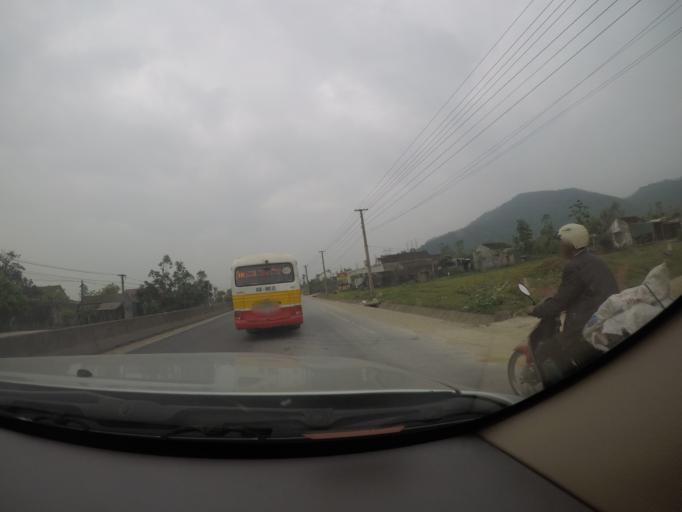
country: VN
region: Ha Tinh
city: Ky Anh
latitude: 18.1379
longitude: 106.2522
